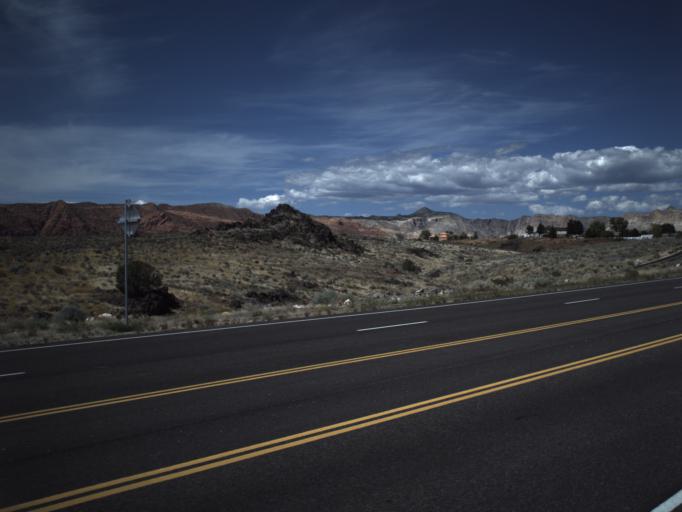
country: US
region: Utah
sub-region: Washington County
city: Santa Clara
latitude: 37.1761
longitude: -113.6188
